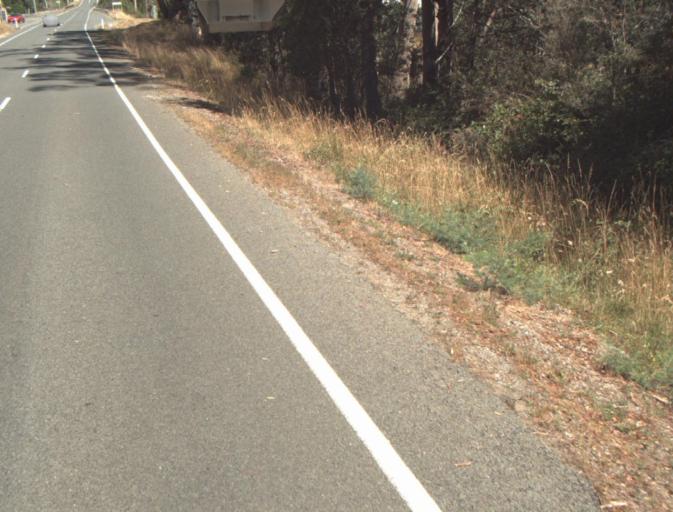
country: AU
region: Tasmania
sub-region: Launceston
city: Newstead
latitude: -41.3881
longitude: 147.3037
